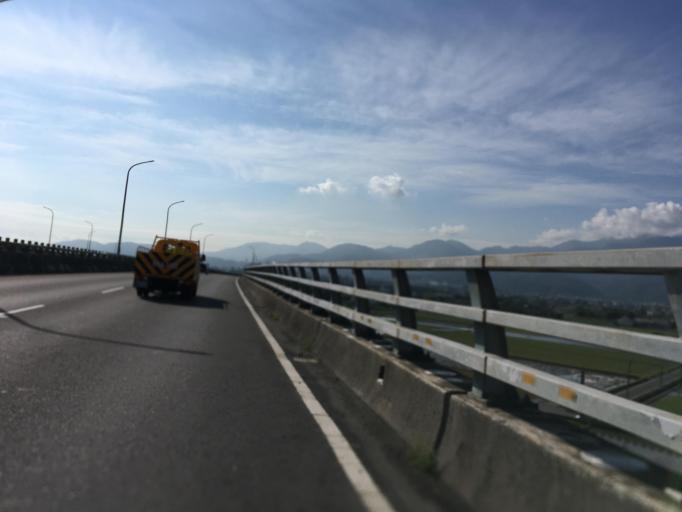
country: TW
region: Taiwan
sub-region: Yilan
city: Yilan
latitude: 24.6591
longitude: 121.8021
